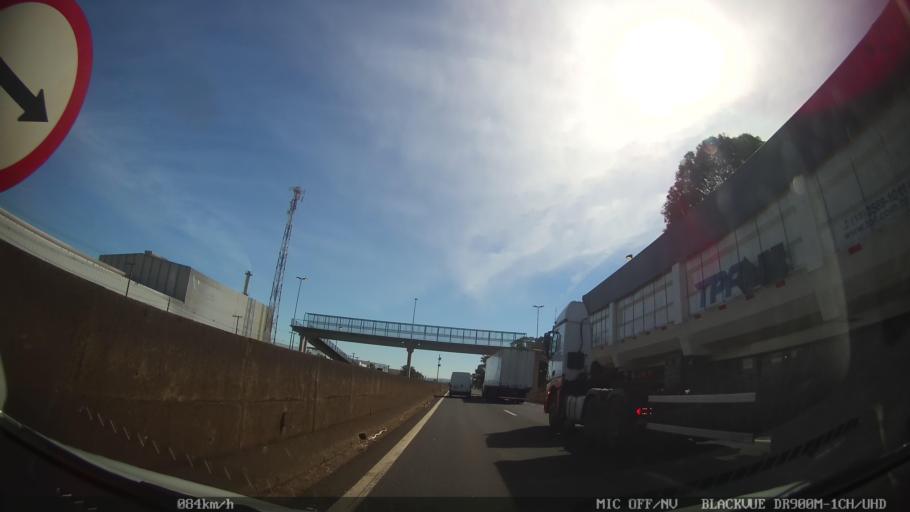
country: BR
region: Sao Paulo
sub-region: Porto Ferreira
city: Porto Ferreira
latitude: -21.8586
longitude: -47.4933
